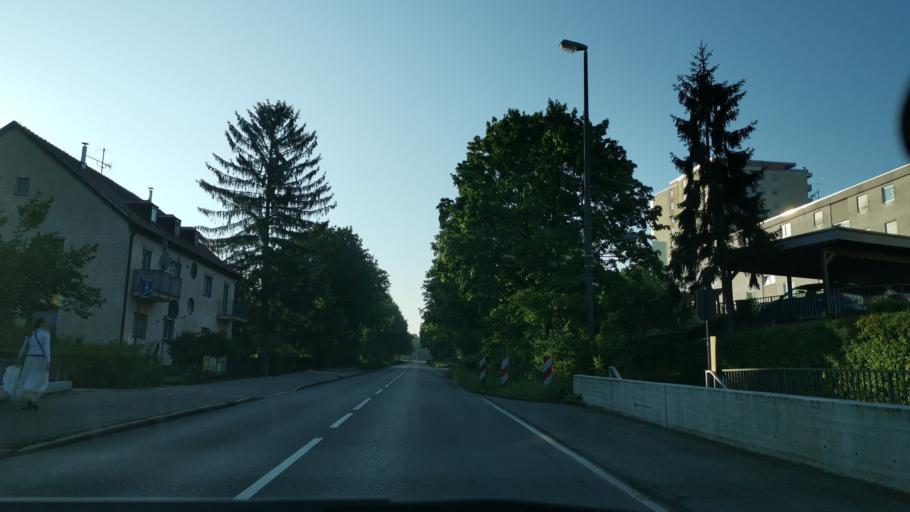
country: DE
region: Baden-Wuerttemberg
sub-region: Regierungsbezirk Stuttgart
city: Boeblingen
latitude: 48.6776
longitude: 9.0247
